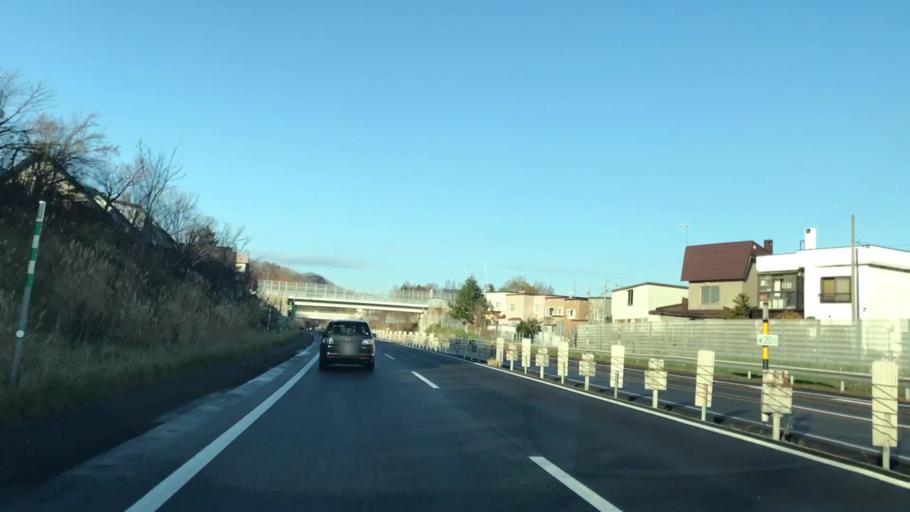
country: JP
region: Hokkaido
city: Sapporo
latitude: 43.1249
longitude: 141.2086
